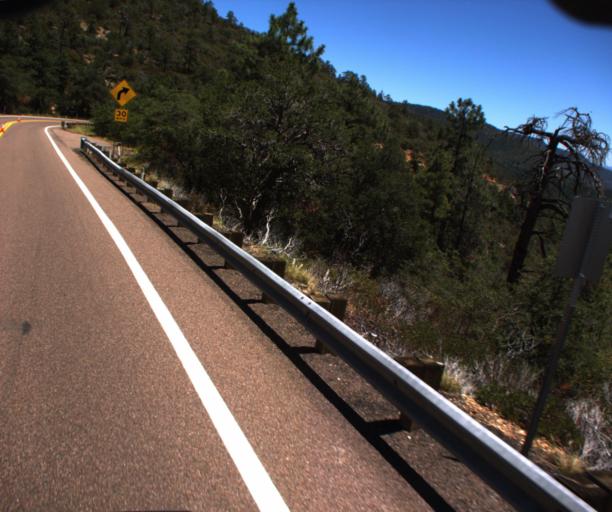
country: US
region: Arizona
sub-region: Gila County
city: Pine
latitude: 34.4213
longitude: -111.5101
